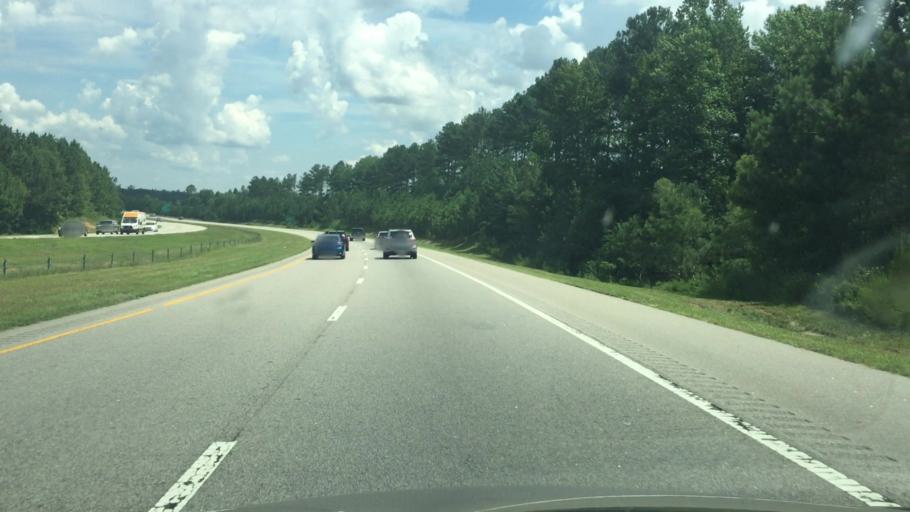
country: US
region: North Carolina
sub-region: Richmond County
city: Ellerbe
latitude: 35.0613
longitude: -79.7412
